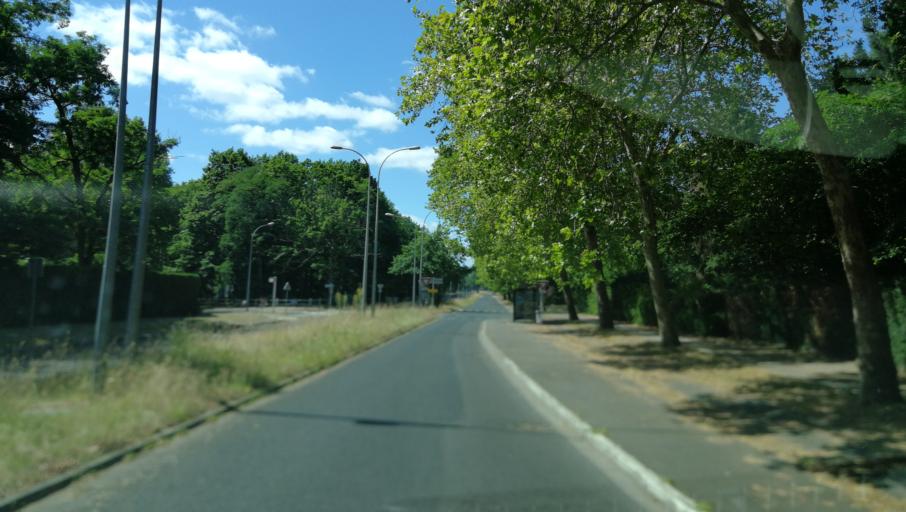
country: FR
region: Centre
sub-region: Departement du Loiret
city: Saint-Cyr-en-Val
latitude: 47.8234
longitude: 1.9321
